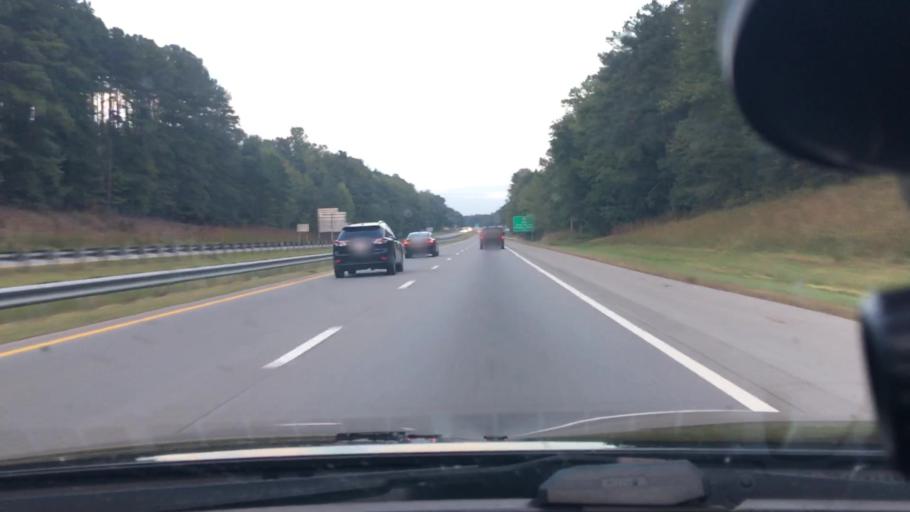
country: US
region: North Carolina
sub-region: Wake County
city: Apex
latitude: 35.7037
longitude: -78.8582
